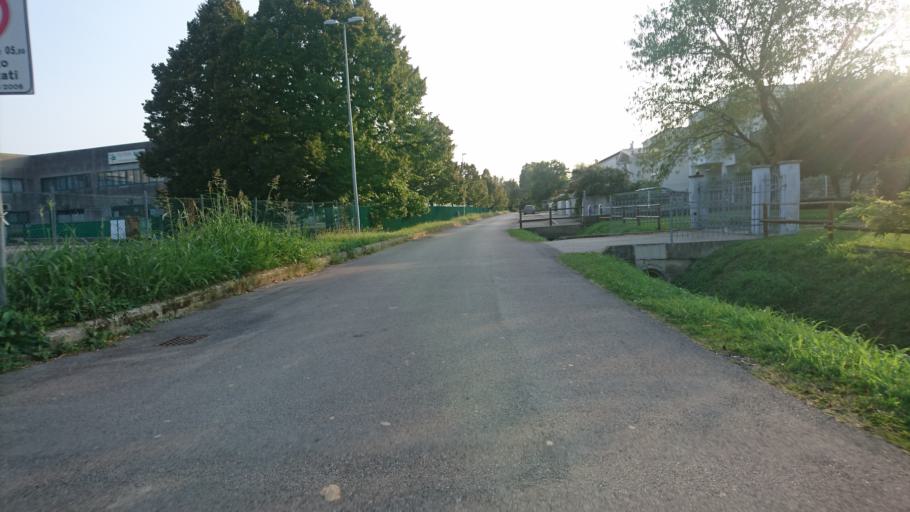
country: IT
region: Veneto
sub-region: Provincia di Padova
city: Limena
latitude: 45.4688
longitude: 11.8418
